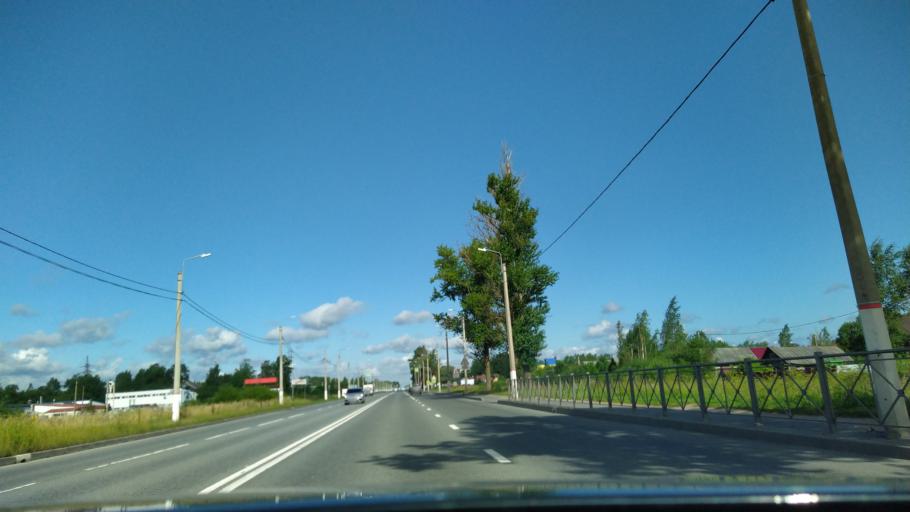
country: RU
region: Leningrad
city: Tosno
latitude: 59.5616
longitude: 30.8393
